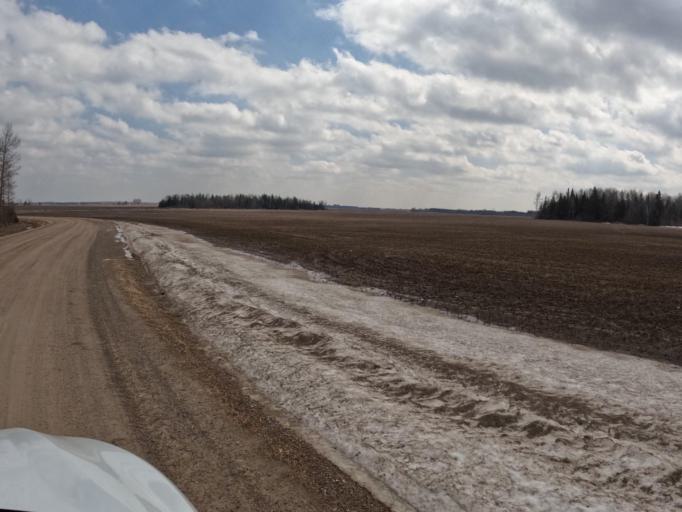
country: CA
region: Ontario
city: Shelburne
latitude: 44.0287
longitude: -80.2542
